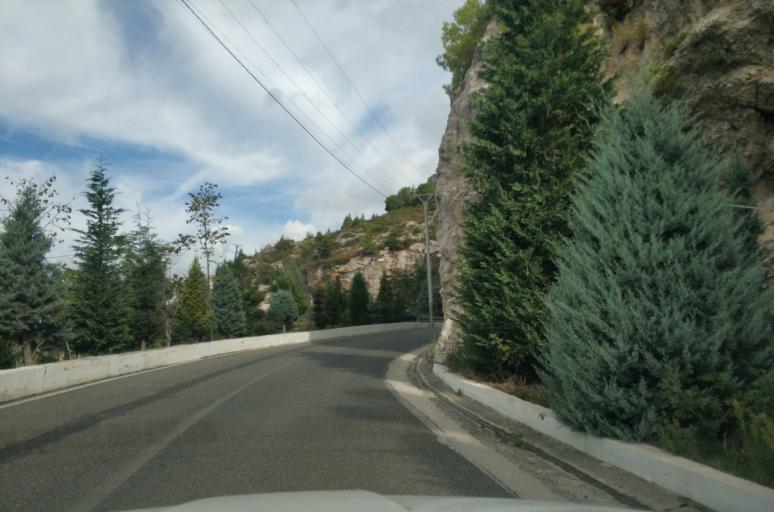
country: AL
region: Durres
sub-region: Rrethi i Krujes
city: Kruje
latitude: 41.5194
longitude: 19.7942
